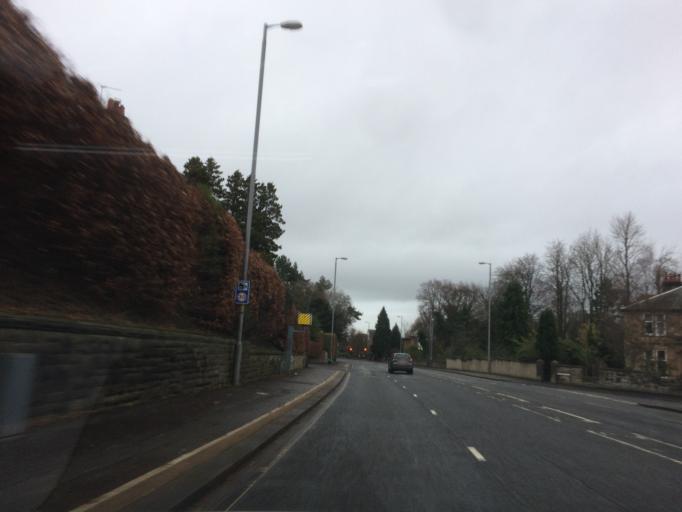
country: GB
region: Scotland
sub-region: East Renfrewshire
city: Giffnock
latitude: 55.7988
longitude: -4.2964
